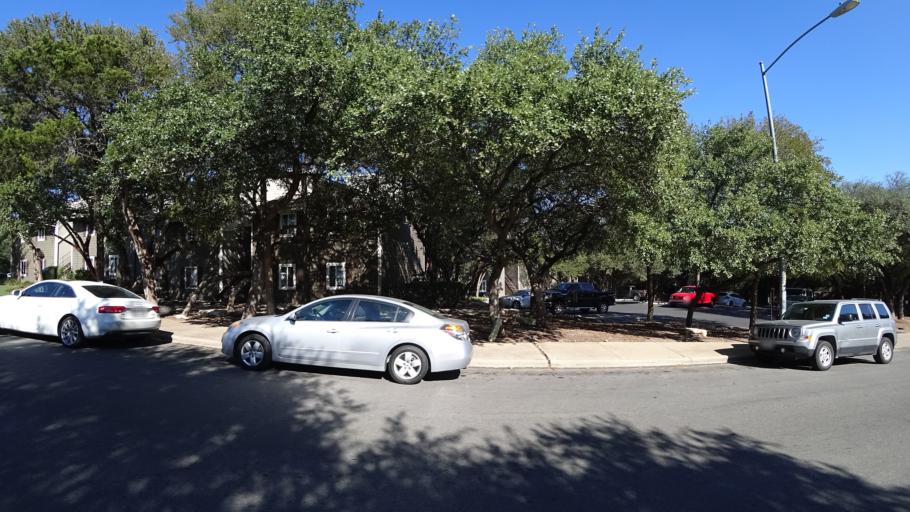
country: US
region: Texas
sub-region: Travis County
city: Rollingwood
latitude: 30.2590
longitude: -97.7910
